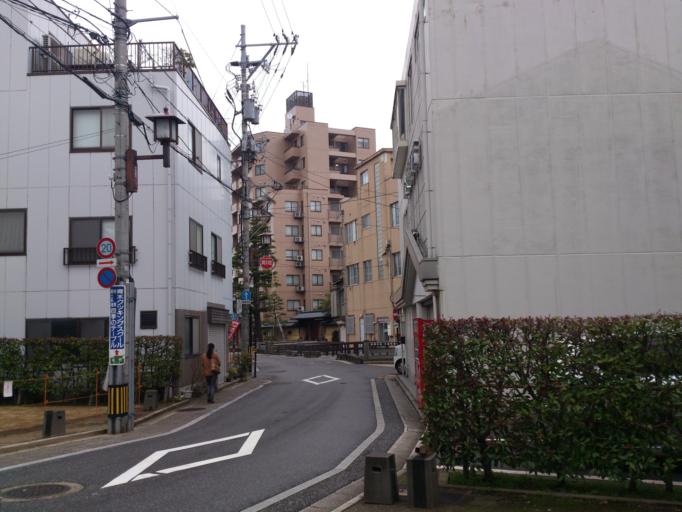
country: JP
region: Ishikawa
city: Kanazawa-shi
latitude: 36.5619
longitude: 136.6503
